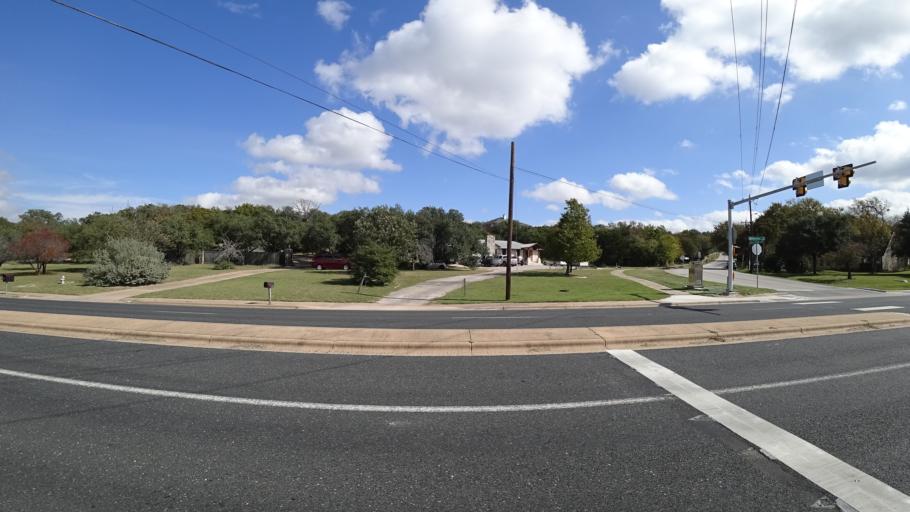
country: US
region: Texas
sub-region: Williamson County
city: Jollyville
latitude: 30.4255
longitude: -97.7851
